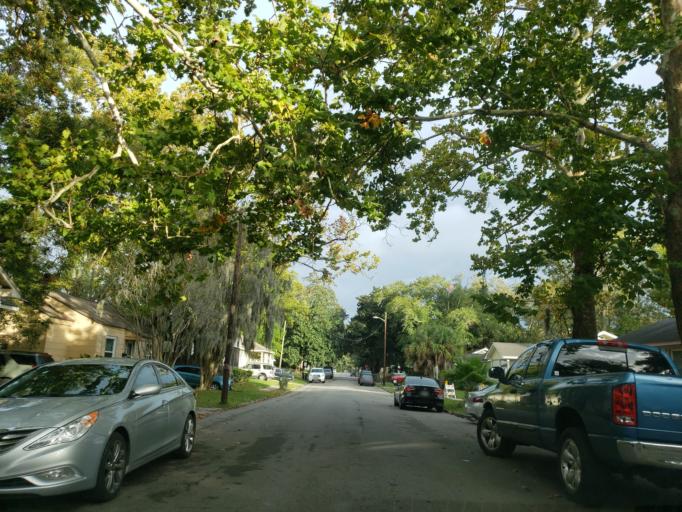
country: US
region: Georgia
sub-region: Chatham County
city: Savannah
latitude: 32.0595
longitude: -81.0767
